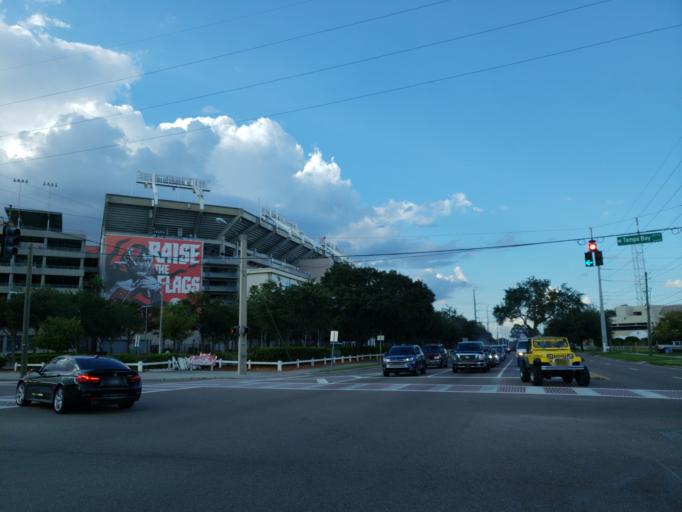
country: US
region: Florida
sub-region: Hillsborough County
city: Egypt Lake-Leto
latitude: 27.9739
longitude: -82.5015
